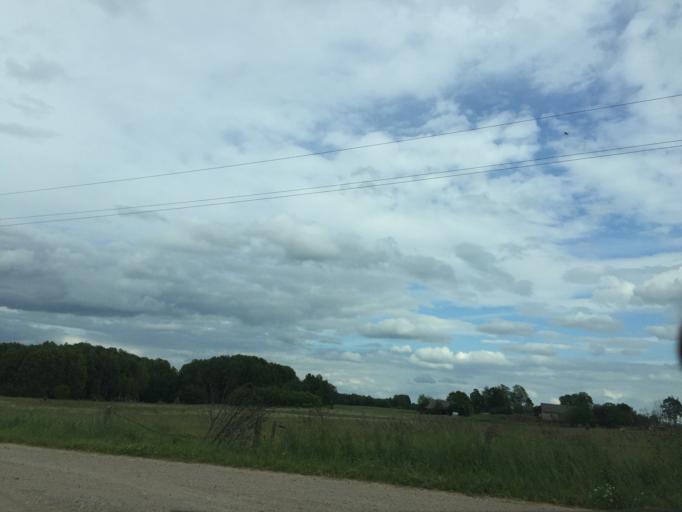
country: LV
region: Apes Novads
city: Ape
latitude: 57.4484
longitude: 26.3515
